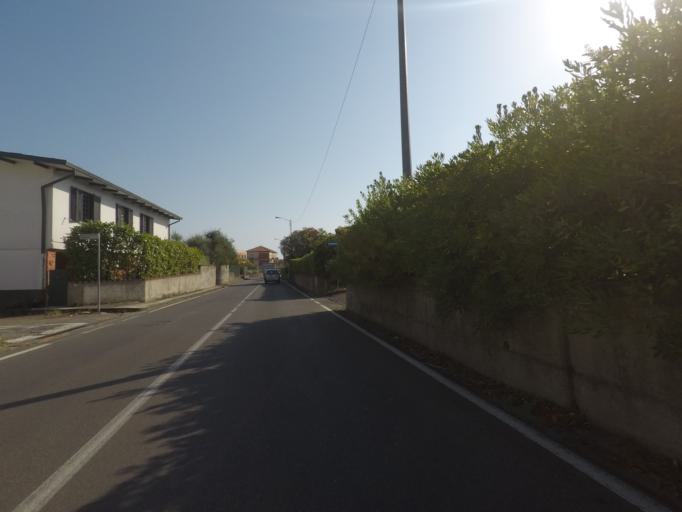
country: IT
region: Liguria
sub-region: Provincia di La Spezia
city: Casano-Dogana-Isola
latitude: 44.0732
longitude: 10.0262
